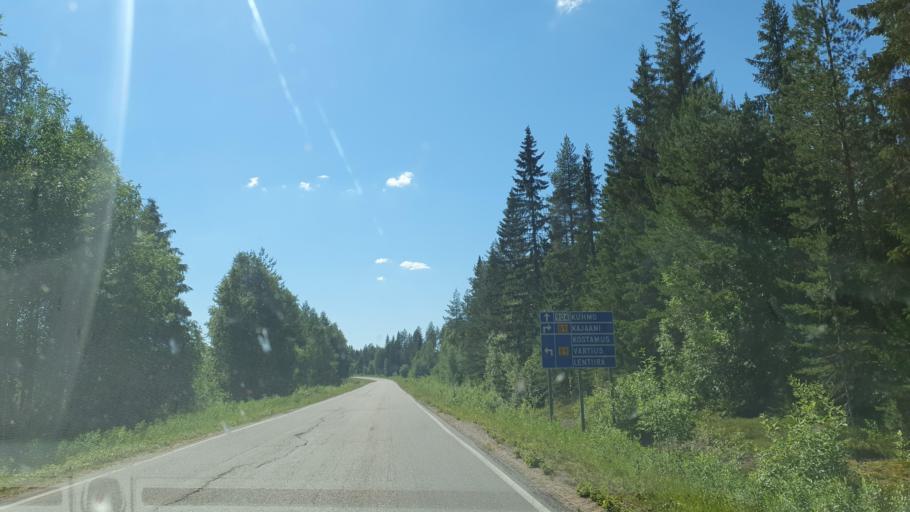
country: FI
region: Kainuu
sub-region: Kehys-Kainuu
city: Suomussalmi
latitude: 64.4435
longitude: 29.0709
